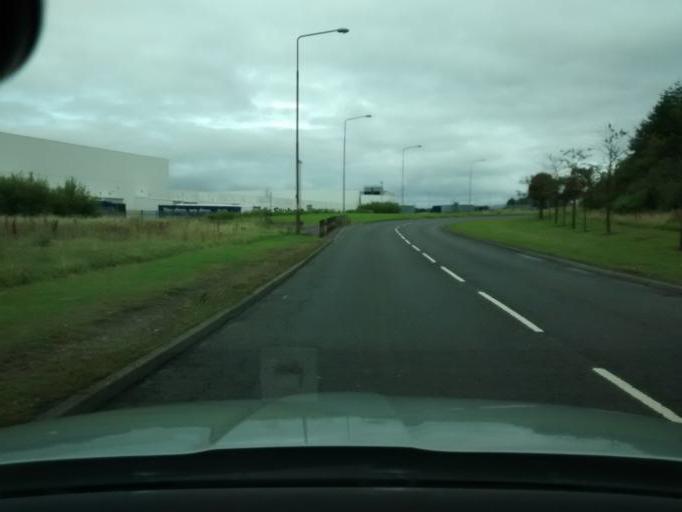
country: GB
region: Scotland
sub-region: West Lothian
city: West Calder
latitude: 55.9009
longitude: -3.5867
